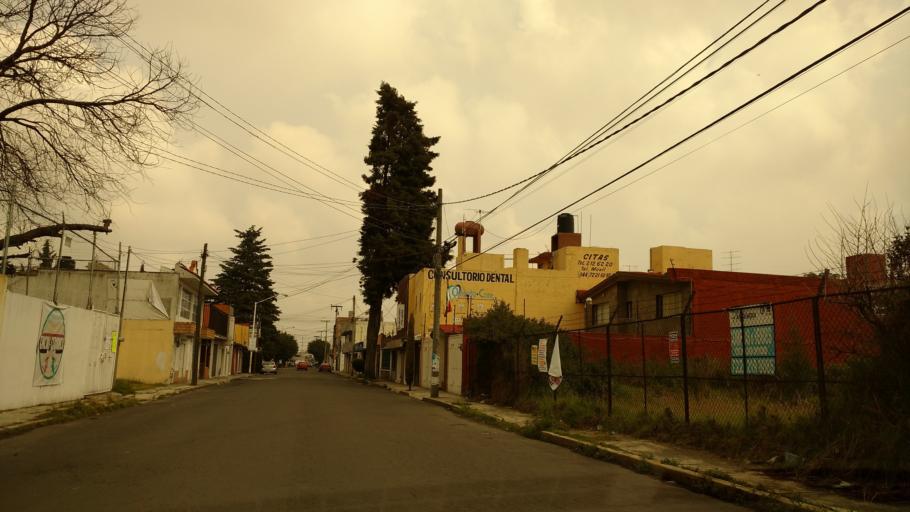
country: MX
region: Mexico
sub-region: Metepec
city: San Jorge Pueblo Nuevo
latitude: 19.2620
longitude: -99.6347
